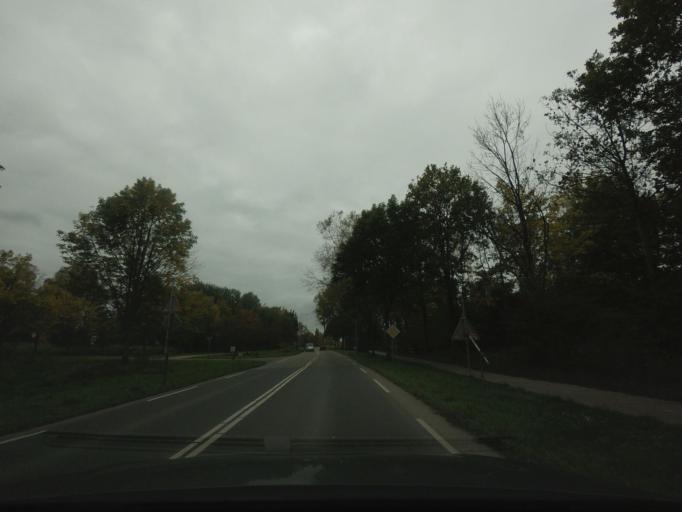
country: NL
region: North Holland
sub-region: Gemeente Heerhugowaard
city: Heerhugowaard
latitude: 52.6761
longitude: 4.8646
